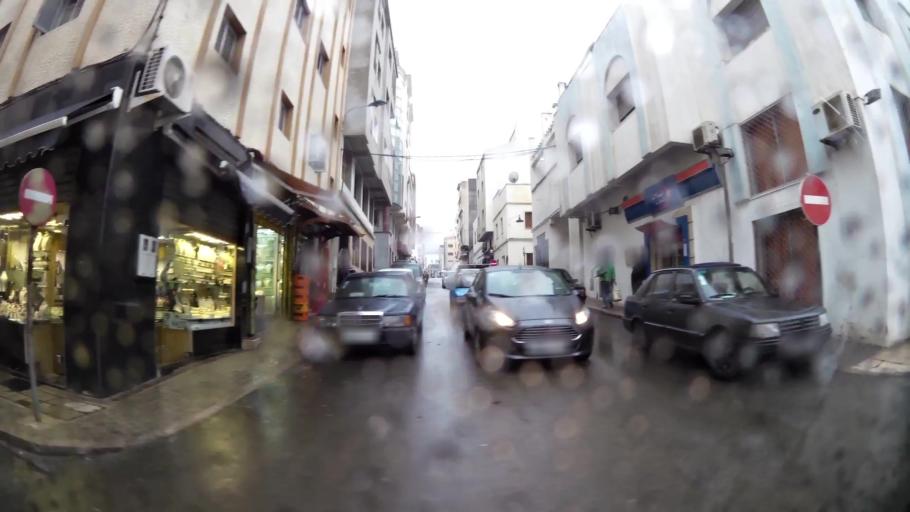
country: MA
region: Taza-Al Hoceima-Taounate
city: Al Hoceima
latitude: 35.2436
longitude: -3.9314
